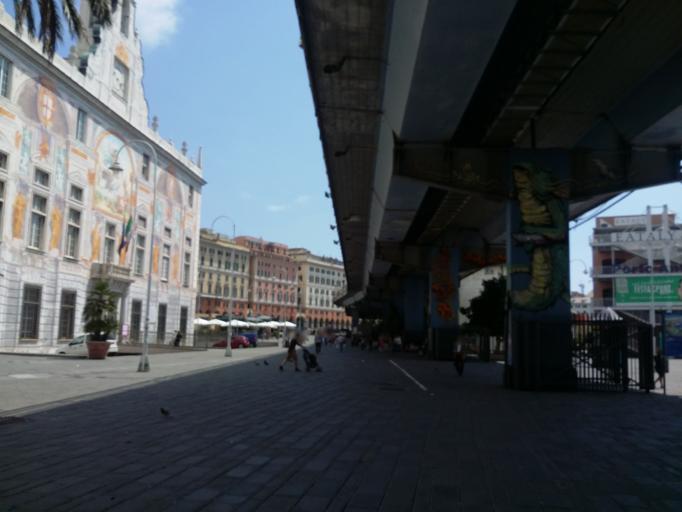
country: IT
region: Liguria
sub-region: Provincia di Genova
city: San Teodoro
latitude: 44.4097
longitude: 8.9283
